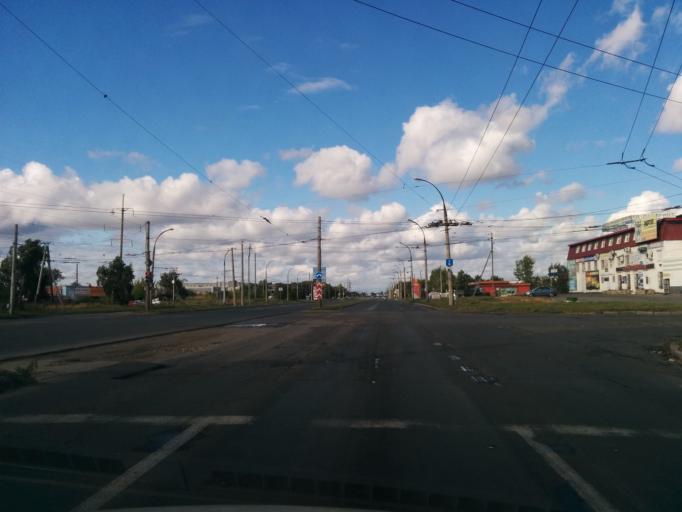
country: RU
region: Samara
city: Tol'yatti
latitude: 53.5390
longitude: 49.2638
